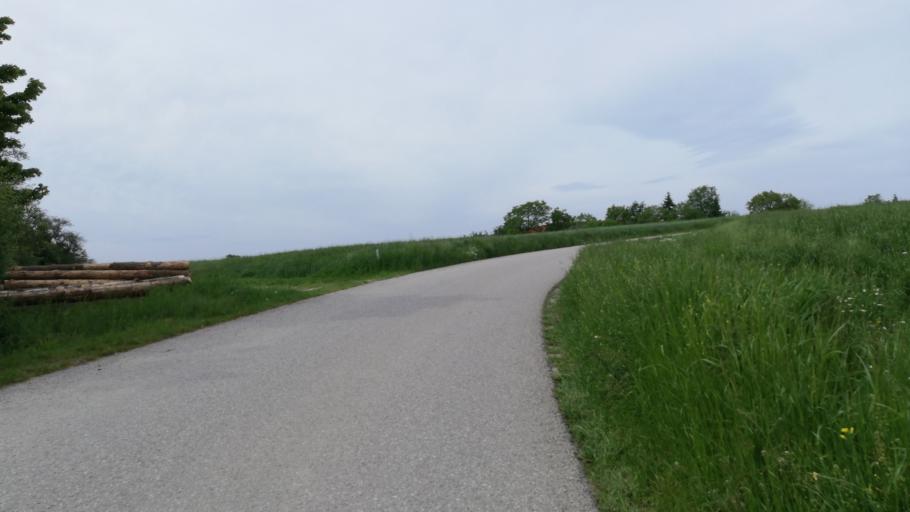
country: AT
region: Upper Austria
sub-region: Wels-Land
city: Gunskirchen
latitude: 48.1770
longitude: 13.9266
